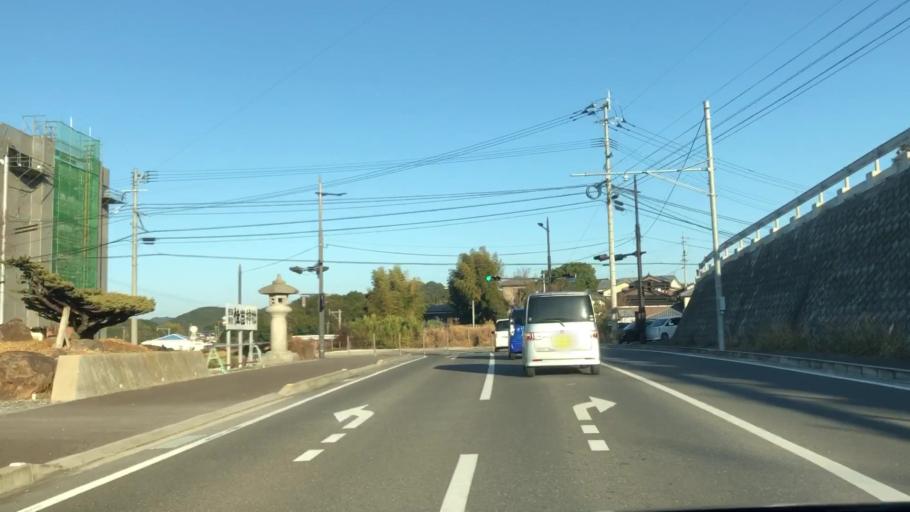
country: JP
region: Nagasaki
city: Sasebo
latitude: 33.1272
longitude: 129.7979
